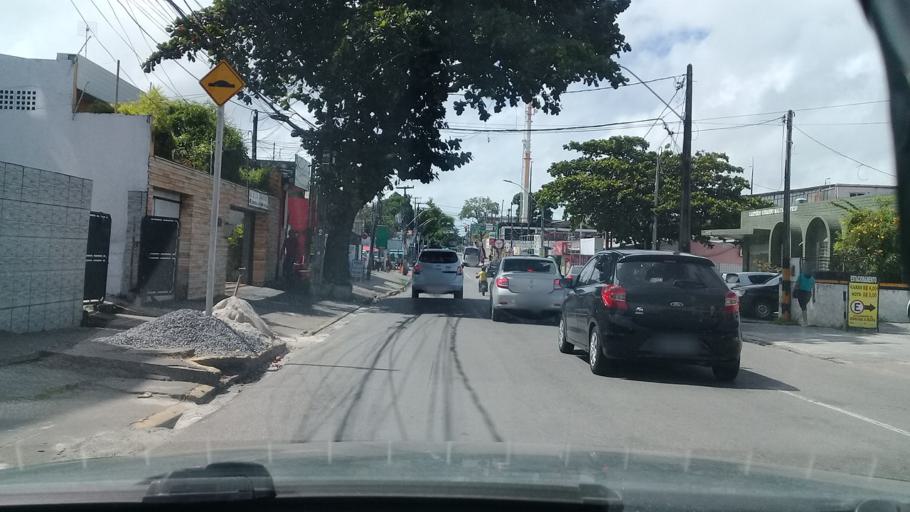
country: BR
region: Pernambuco
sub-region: Jaboatao Dos Guararapes
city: Jaboatao
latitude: -8.1648
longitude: -34.9193
